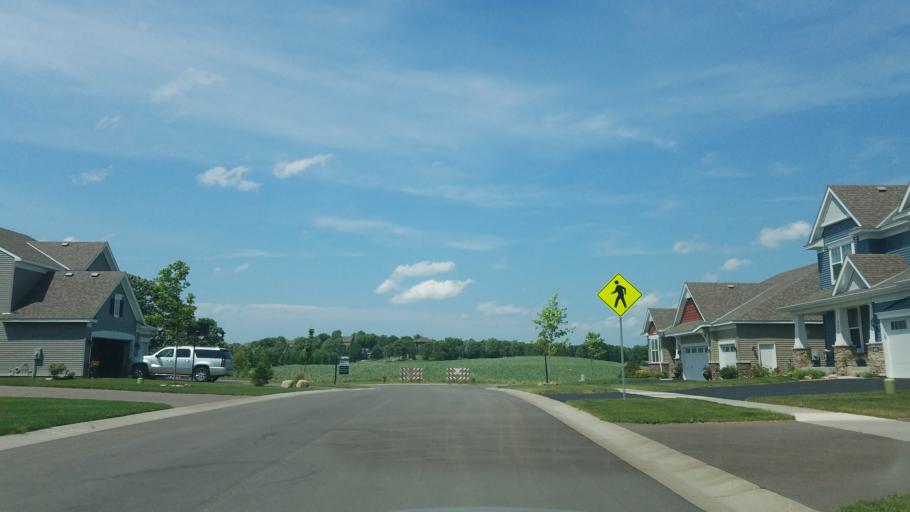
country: US
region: Minnesota
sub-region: Washington County
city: Woodbury
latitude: 44.8865
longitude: -92.9230
